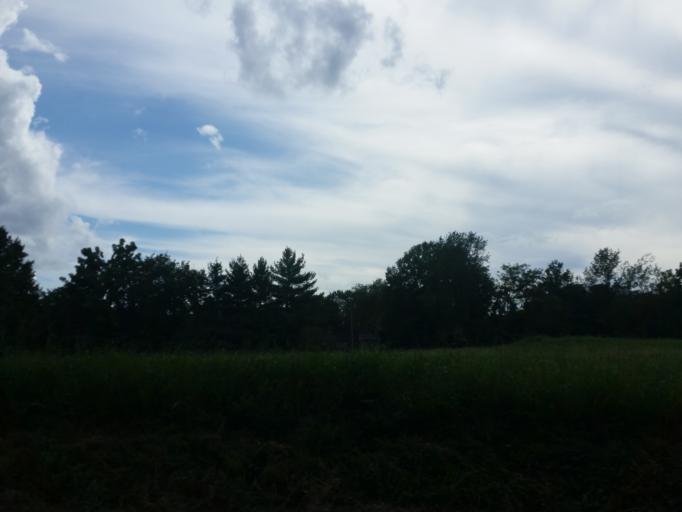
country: US
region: Kentucky
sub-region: Christian County
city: Hopkinsville
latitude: 36.8493
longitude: -87.5131
